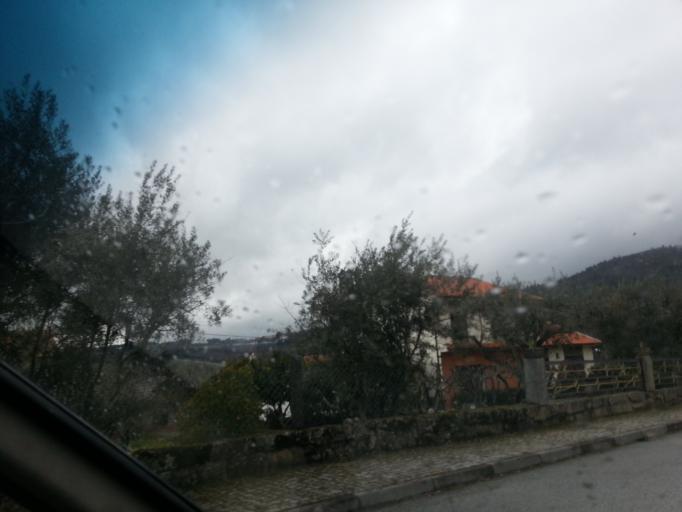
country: PT
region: Guarda
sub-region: Fornos de Algodres
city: Fornos de Algodres
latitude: 40.6189
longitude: -7.5861
